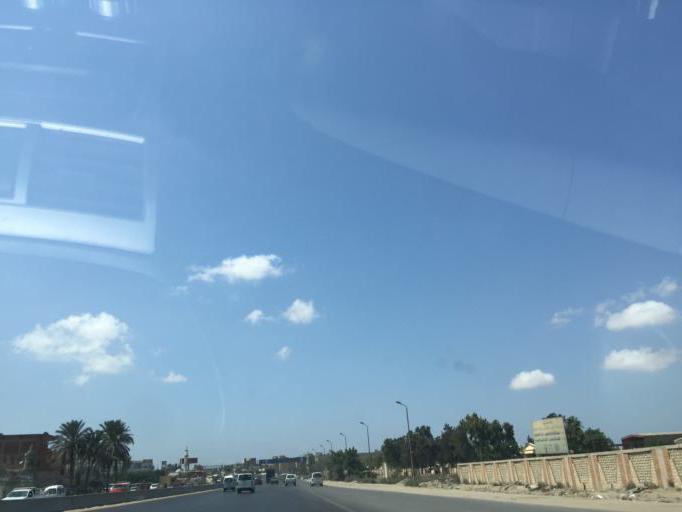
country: EG
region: Alexandria
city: Alexandria
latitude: 31.0202
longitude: 29.7943
